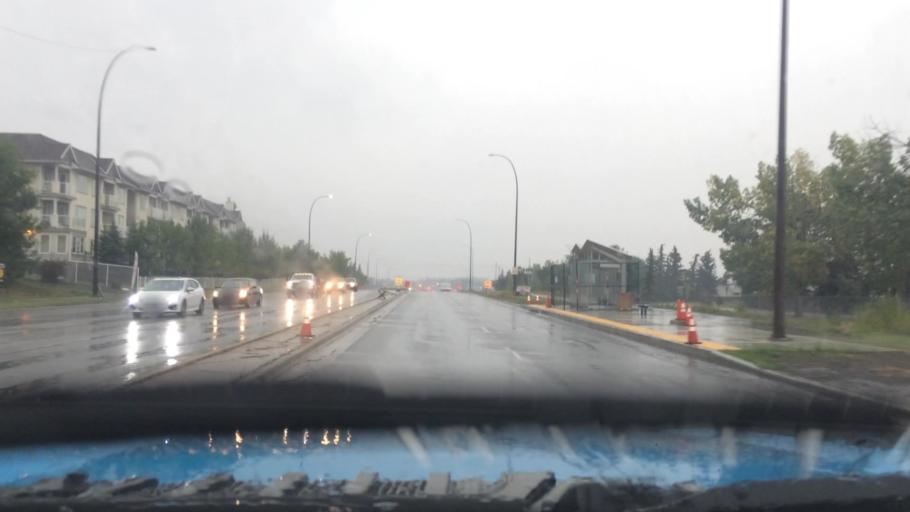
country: CA
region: Alberta
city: Calgary
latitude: 51.0914
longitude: -113.9584
